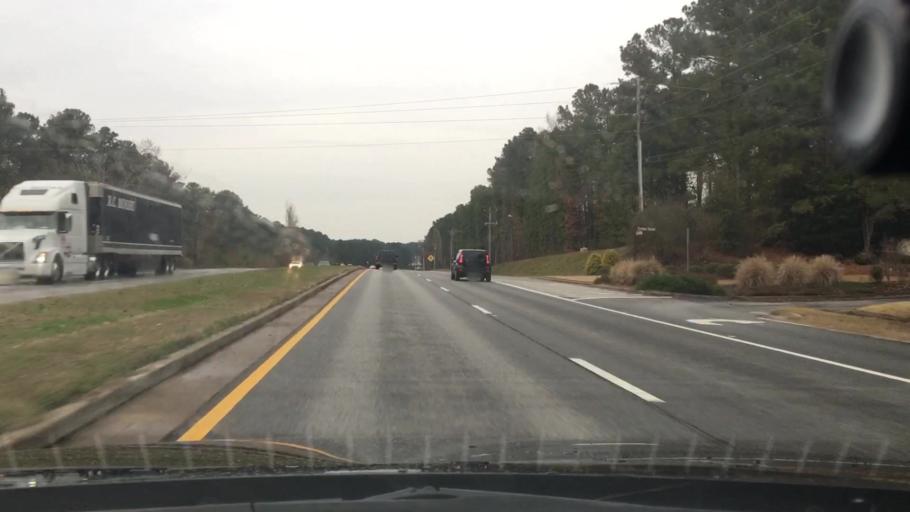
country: US
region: Georgia
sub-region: Fayette County
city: Peachtree City
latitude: 33.4165
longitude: -84.6030
